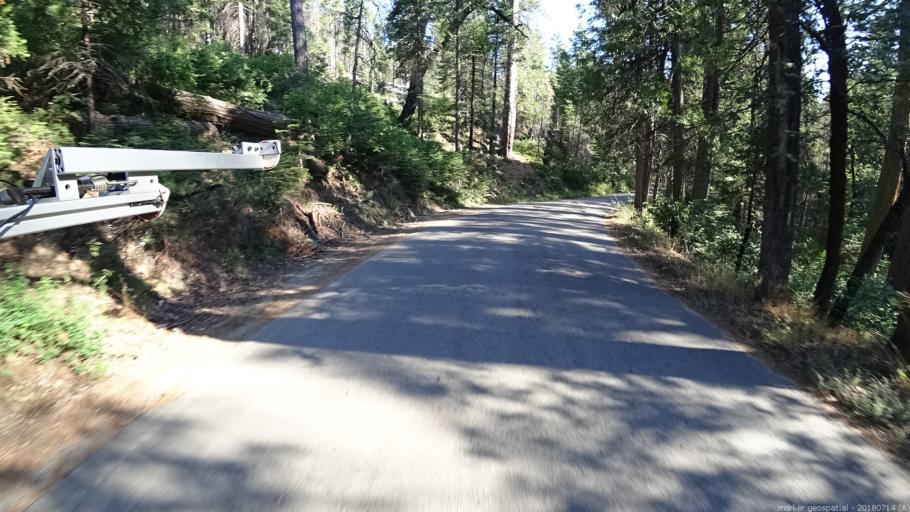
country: US
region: California
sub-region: Madera County
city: Oakhurst
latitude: 37.4346
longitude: -119.6377
